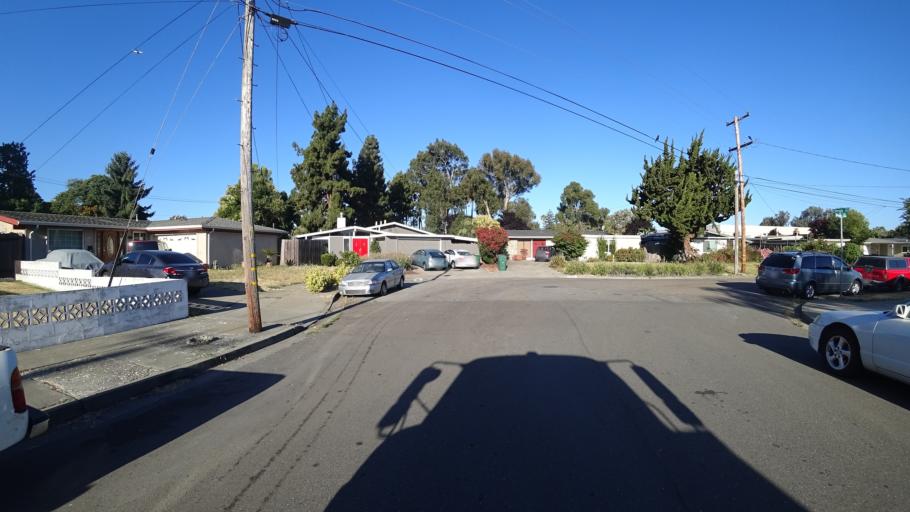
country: US
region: California
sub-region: Alameda County
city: Hayward
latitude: 37.6457
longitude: -122.1033
